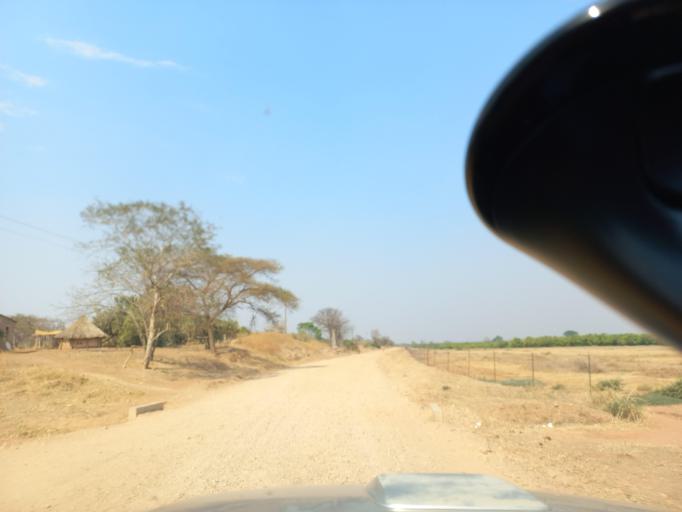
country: ZW
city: Chirundu
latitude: -15.9313
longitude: 28.9533
